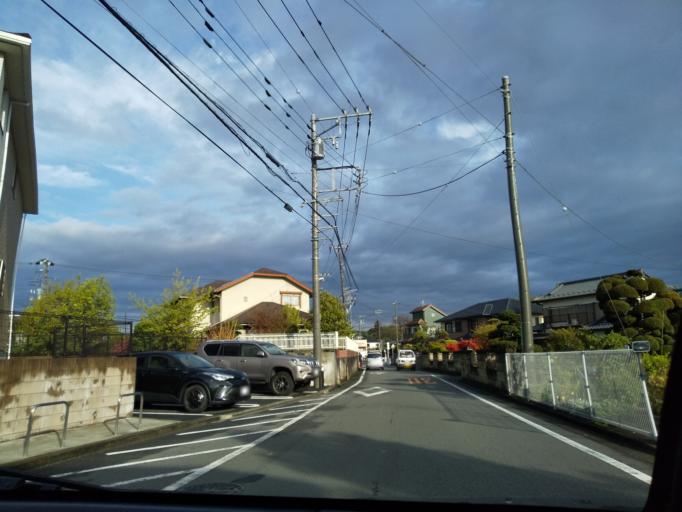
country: JP
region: Tokyo
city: Hachioji
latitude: 35.6035
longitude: 139.3214
